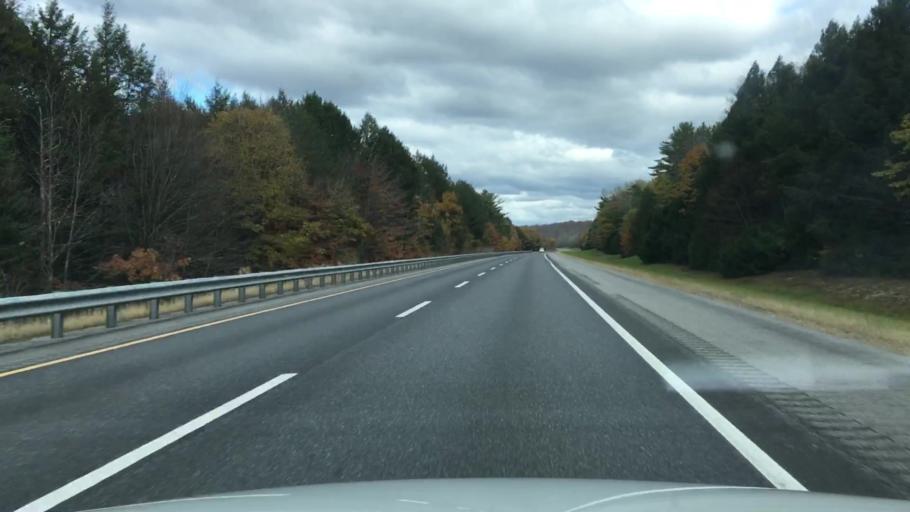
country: US
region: Maine
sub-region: Sagadahoc County
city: Richmond
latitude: 44.0567
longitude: -69.8864
